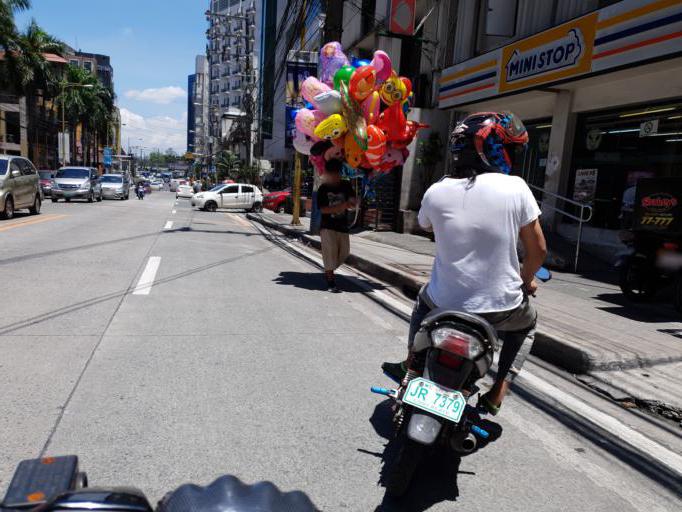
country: PH
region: Metro Manila
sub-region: Makati City
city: Makati City
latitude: 14.5657
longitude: 121.0297
